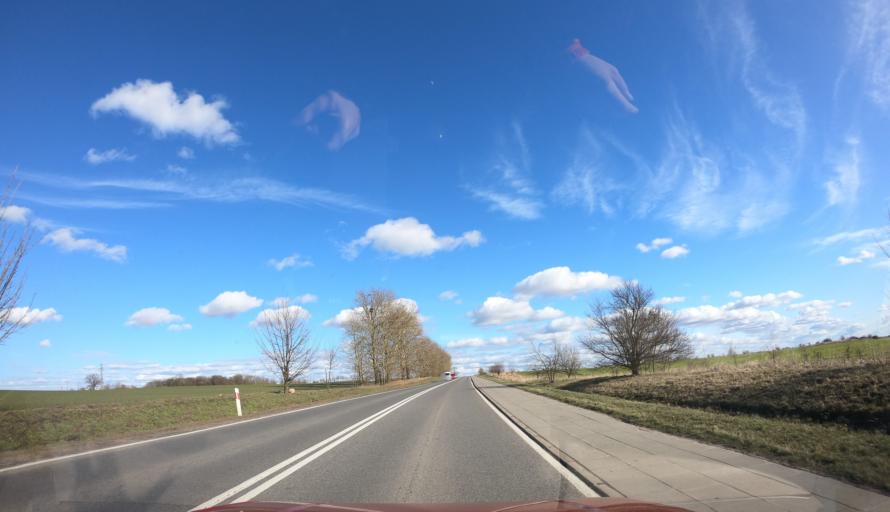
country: PL
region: West Pomeranian Voivodeship
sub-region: Powiat policki
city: Dobra
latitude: 53.4370
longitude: 14.4186
